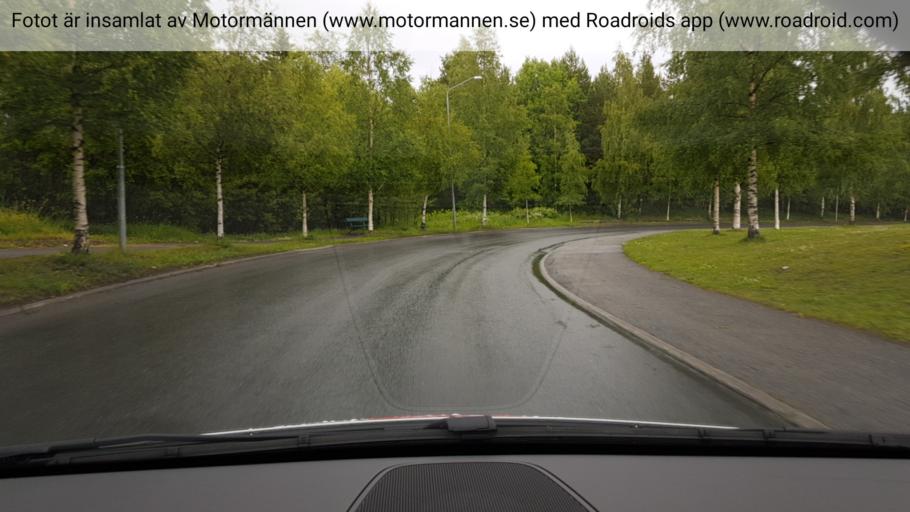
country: SE
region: Jaemtland
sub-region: OEstersunds Kommun
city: Ostersund
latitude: 63.1789
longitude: 14.6828
